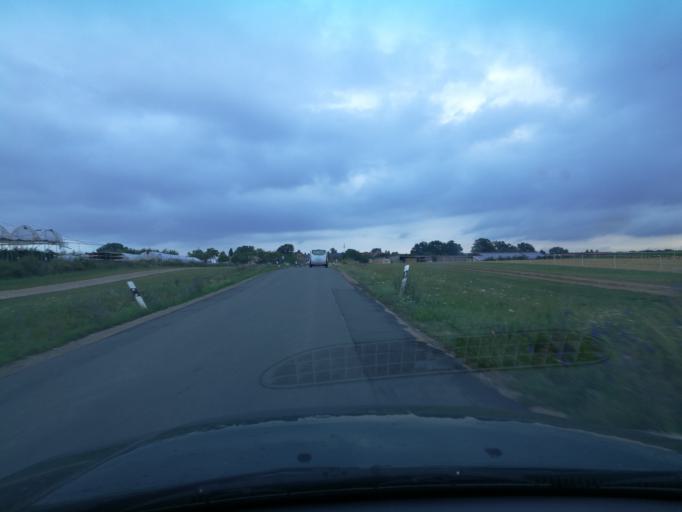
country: DE
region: Bavaria
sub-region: Regierungsbezirk Mittelfranken
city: Obermichelbach
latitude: 49.5349
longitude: 10.9596
